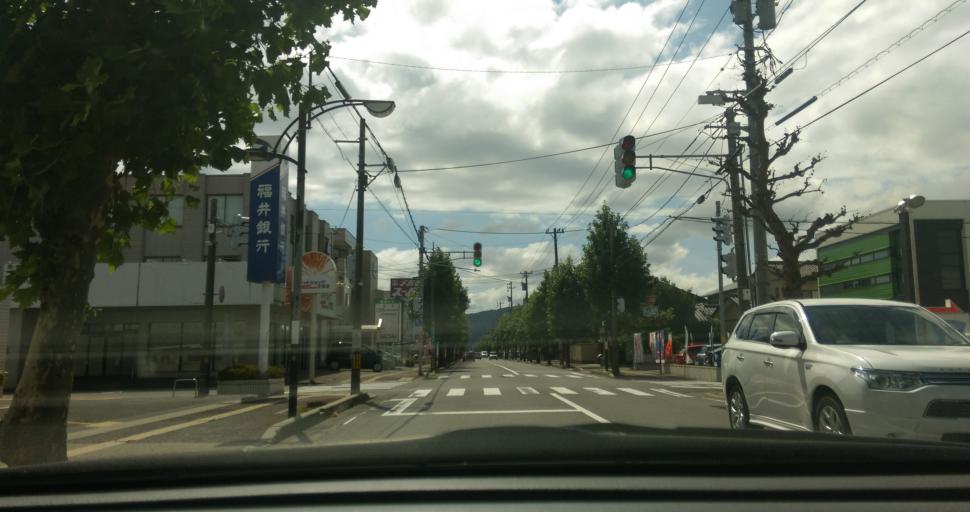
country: JP
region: Fukui
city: Fukui-shi
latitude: 36.0878
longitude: 136.2249
